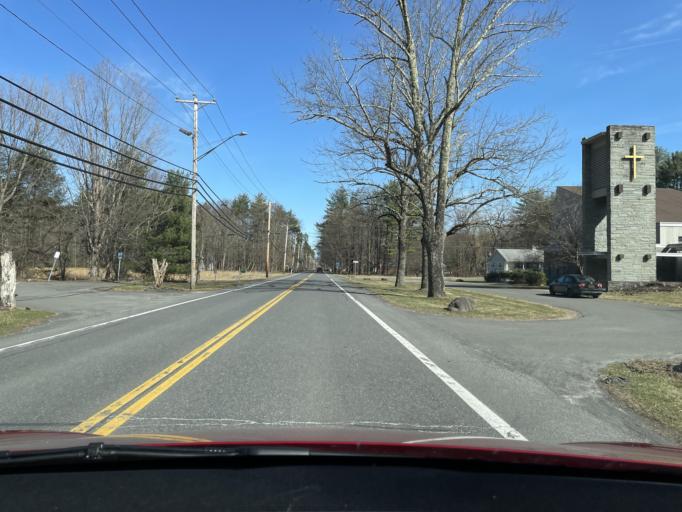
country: US
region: New York
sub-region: Ulster County
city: Woodstock
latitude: 42.0404
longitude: -74.1441
